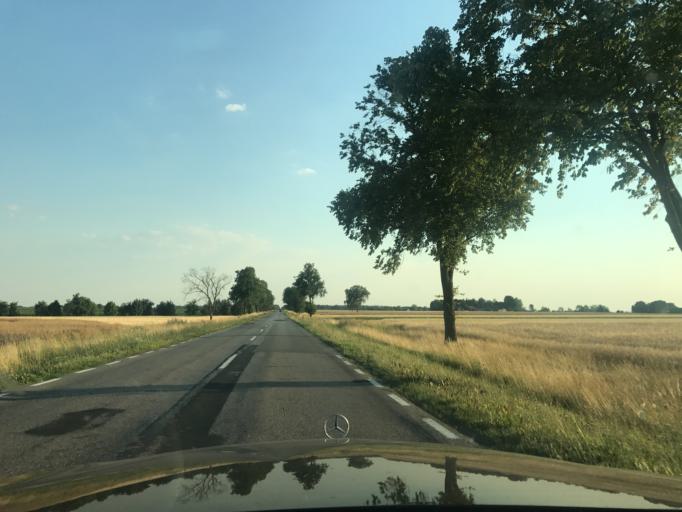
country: PL
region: Lublin Voivodeship
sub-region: Powiat parczewski
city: Jablon
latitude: 51.6827
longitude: 23.0273
